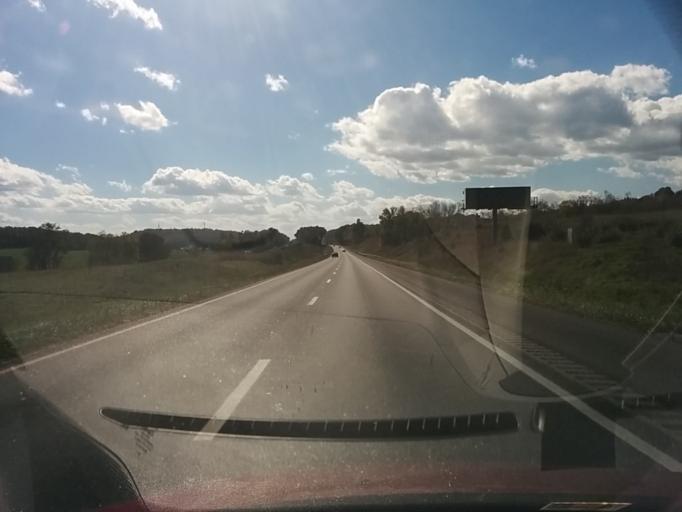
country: US
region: Virginia
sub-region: City of Buena Vista
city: Buena Vista
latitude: 37.9184
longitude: -79.2491
